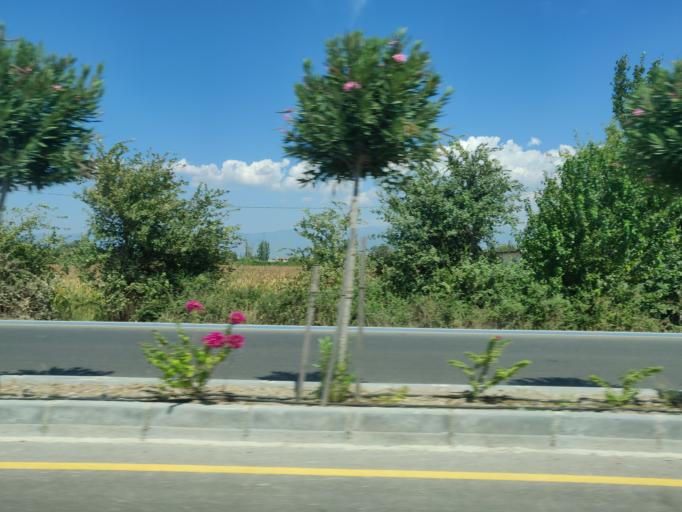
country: TR
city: Dalyan
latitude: 36.8399
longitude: 28.6567
